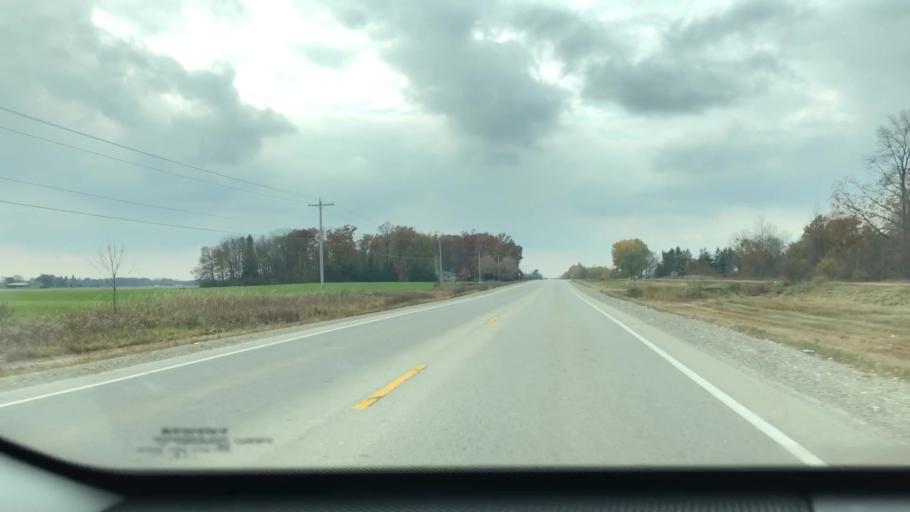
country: US
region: Wisconsin
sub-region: Brown County
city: Oneida
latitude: 44.5020
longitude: -88.2065
